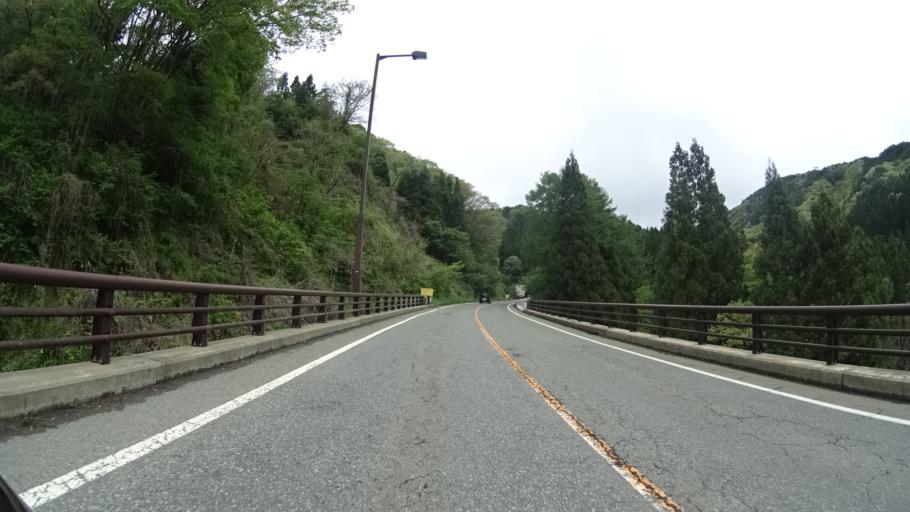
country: JP
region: Nagano
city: Nagano-shi
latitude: 36.7048
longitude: 138.2028
